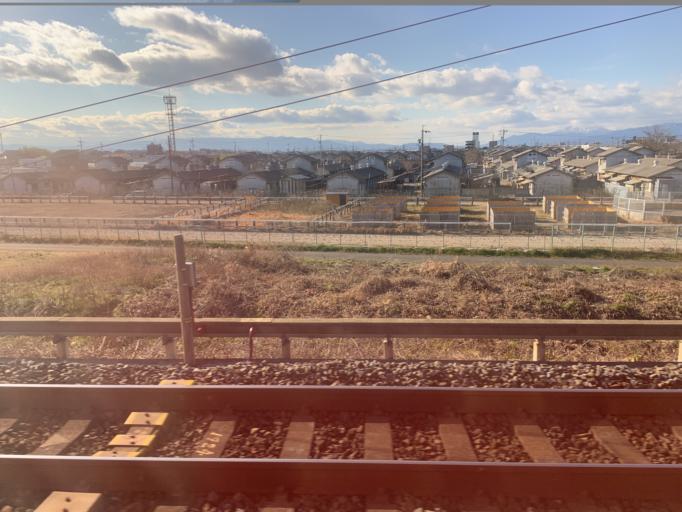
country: JP
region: Gifu
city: Kasamatsucho
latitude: 35.3796
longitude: 136.7807
